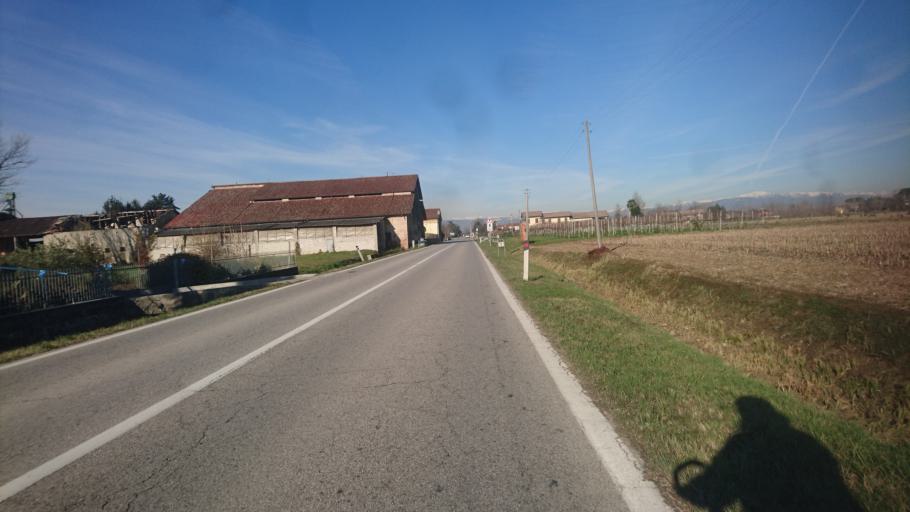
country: IT
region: Veneto
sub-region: Provincia di Padova
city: Villafranca Padovana
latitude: 45.5020
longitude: 11.7933
